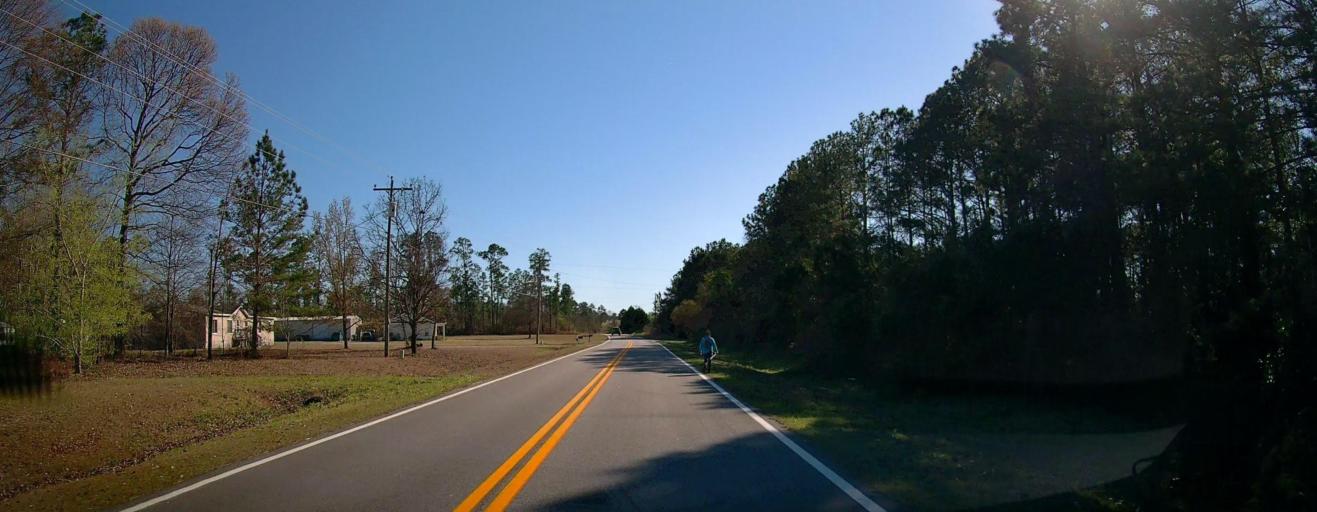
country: US
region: Georgia
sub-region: Peach County
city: Byron
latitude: 32.6823
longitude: -83.8068
